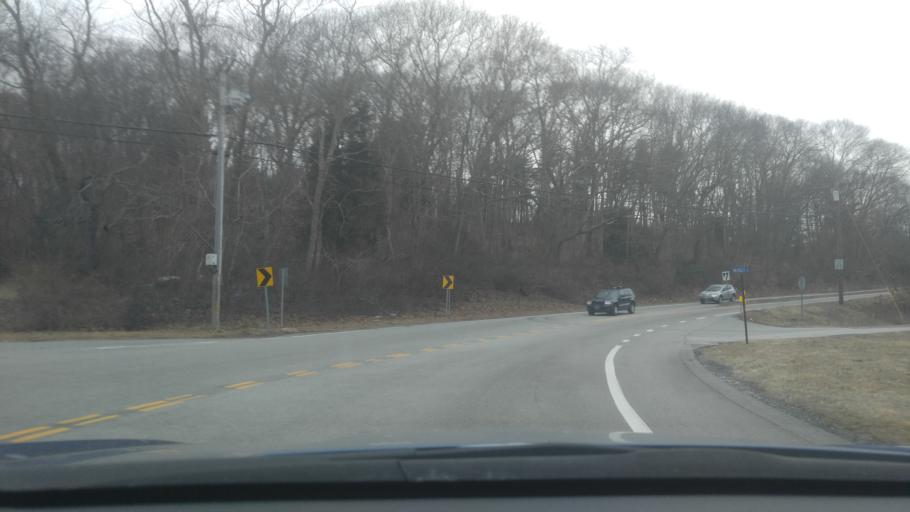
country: US
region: Rhode Island
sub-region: Washington County
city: Narragansett Pier
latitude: 41.4882
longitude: -71.4493
